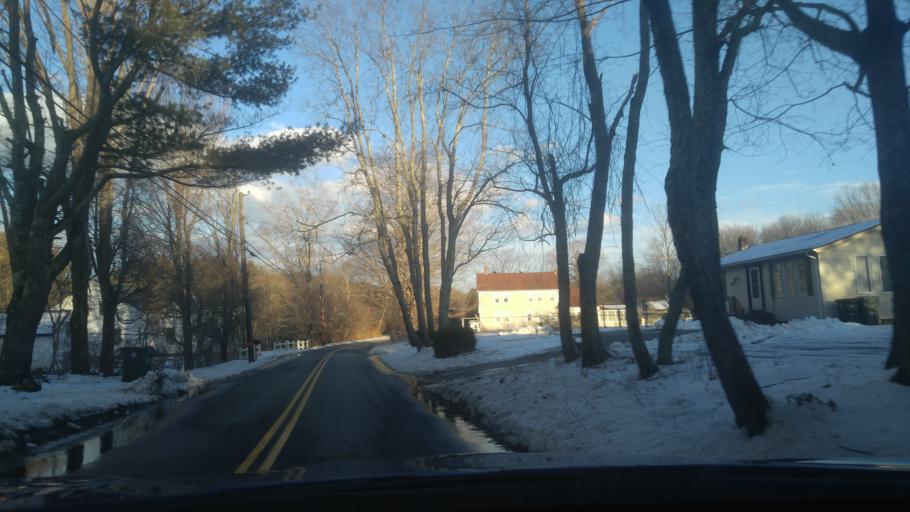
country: US
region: Rhode Island
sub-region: Kent County
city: Coventry
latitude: 41.7190
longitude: -71.6680
